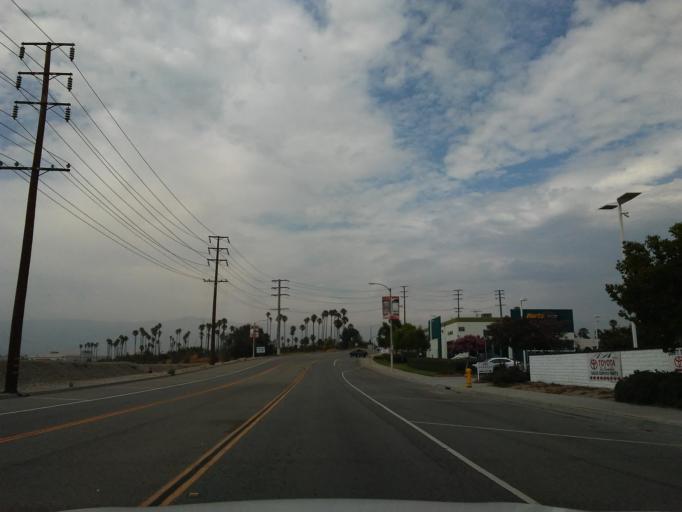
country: US
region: California
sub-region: San Bernardino County
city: Colton
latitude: 34.0751
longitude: -117.2996
